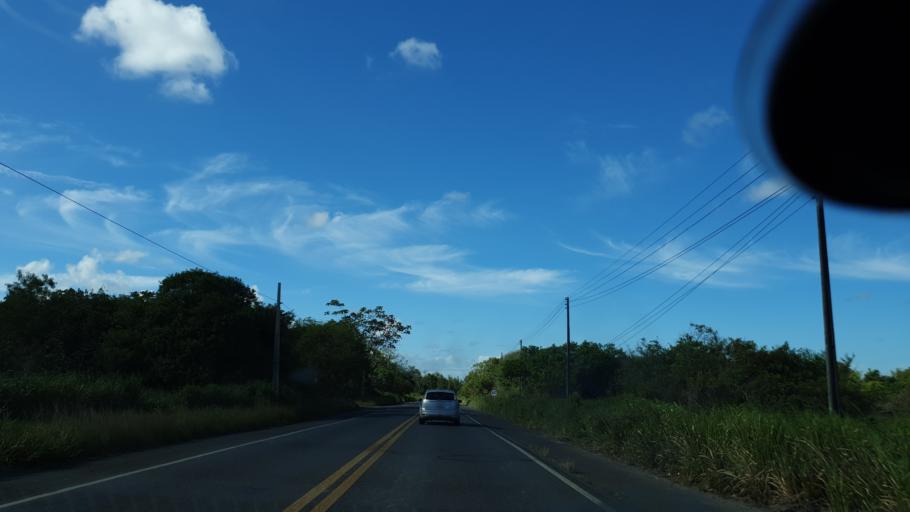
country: BR
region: Bahia
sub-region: Camacari
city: Camacari
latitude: -12.6633
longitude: -38.3015
